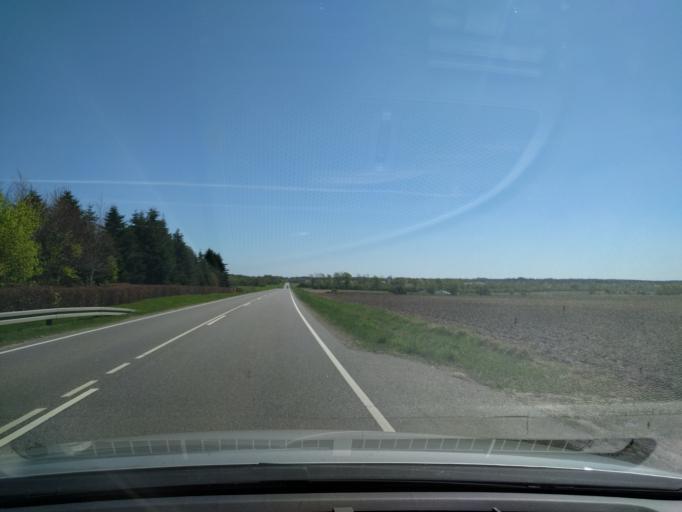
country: DK
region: South Denmark
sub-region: Billund Kommune
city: Billund
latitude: 55.6804
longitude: 9.0233
